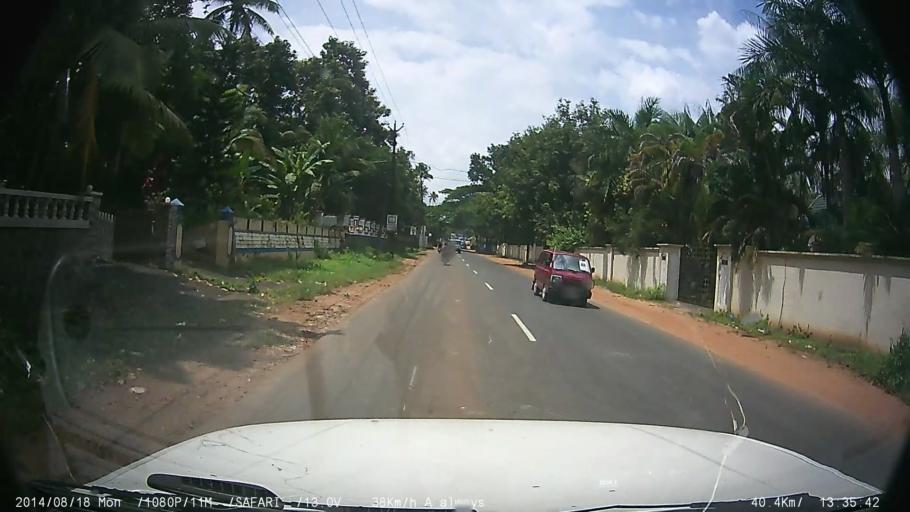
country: IN
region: Kerala
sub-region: Kottayam
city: Kottayam
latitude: 9.6524
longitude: 76.5509
